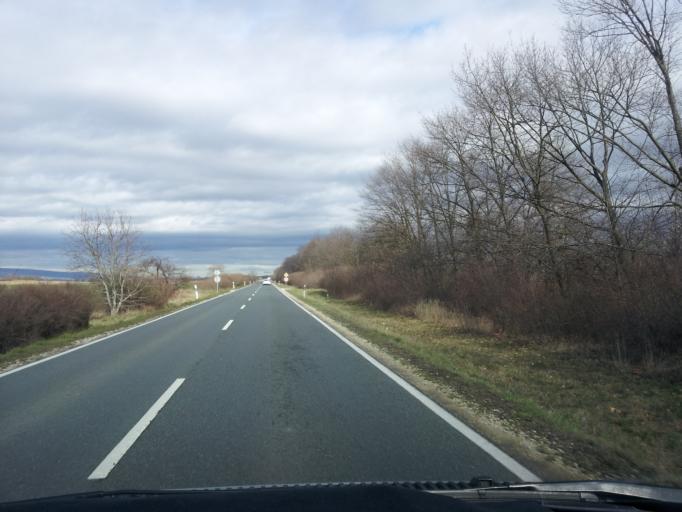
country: HU
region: Vas
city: Gencsapati
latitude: 47.2929
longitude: 16.6085
